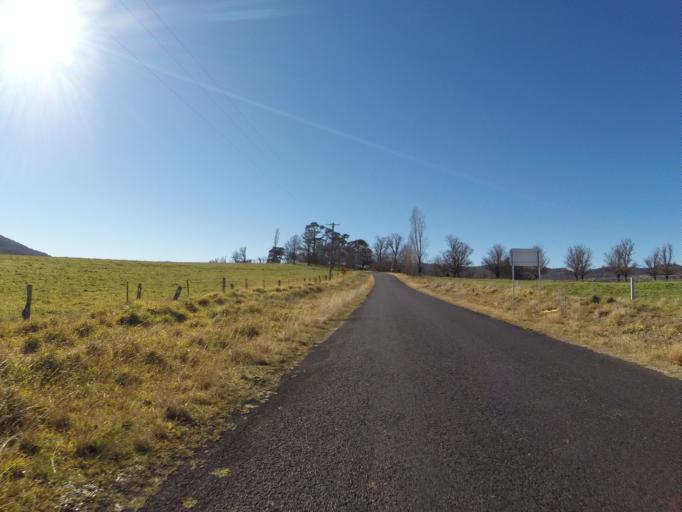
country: AU
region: New South Wales
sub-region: Oberon
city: Oberon
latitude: -33.5392
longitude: 149.8828
